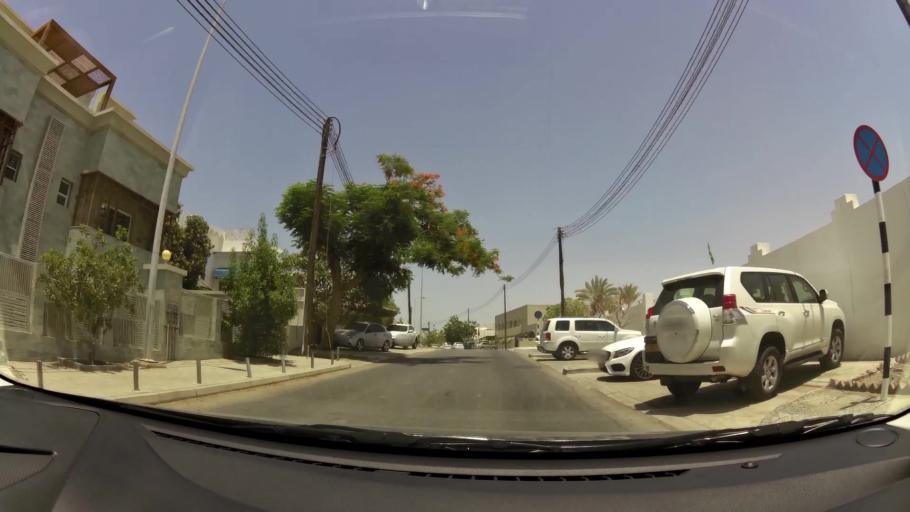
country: OM
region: Muhafazat Masqat
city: Muscat
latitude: 23.6251
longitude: 58.4954
